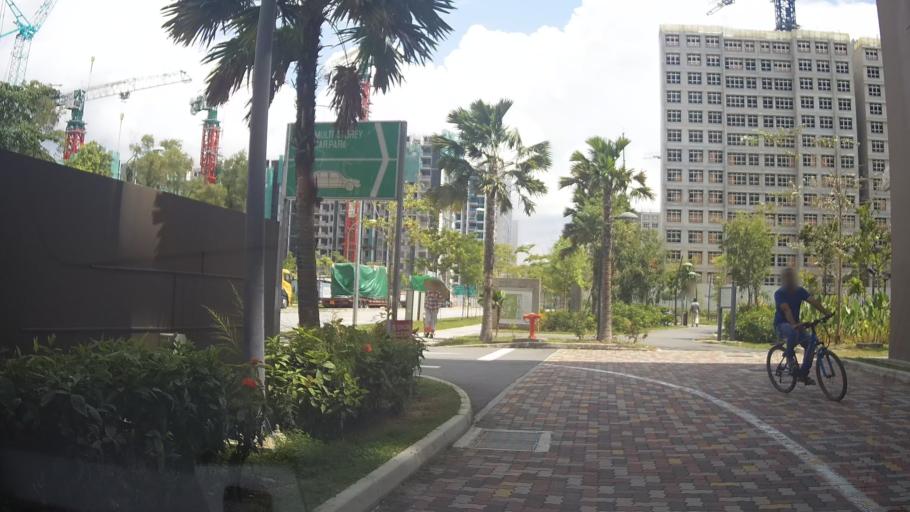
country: SG
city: Singapore
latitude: 1.3521
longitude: 103.9288
